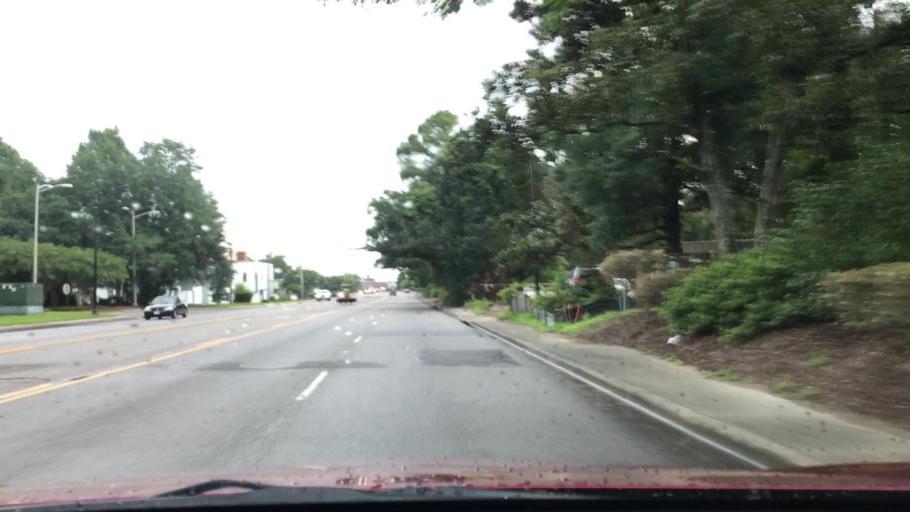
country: US
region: South Carolina
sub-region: Charleston County
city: North Charleston
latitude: 32.8635
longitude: -80.0203
